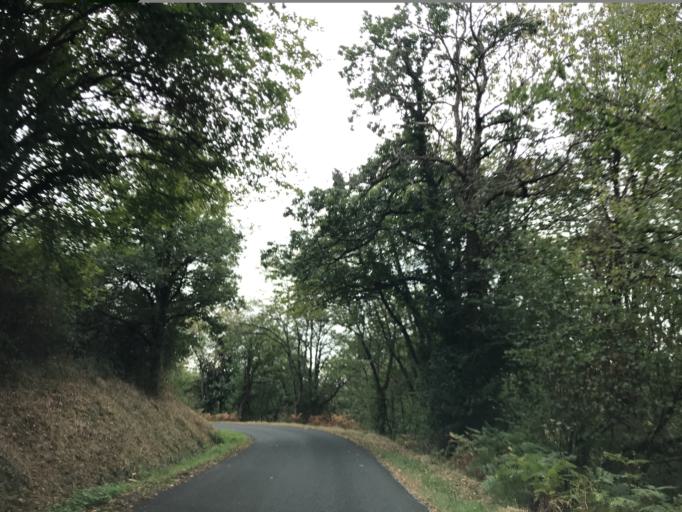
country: FR
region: Auvergne
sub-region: Departement du Puy-de-Dome
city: Escoutoux
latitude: 45.8223
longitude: 3.5930
